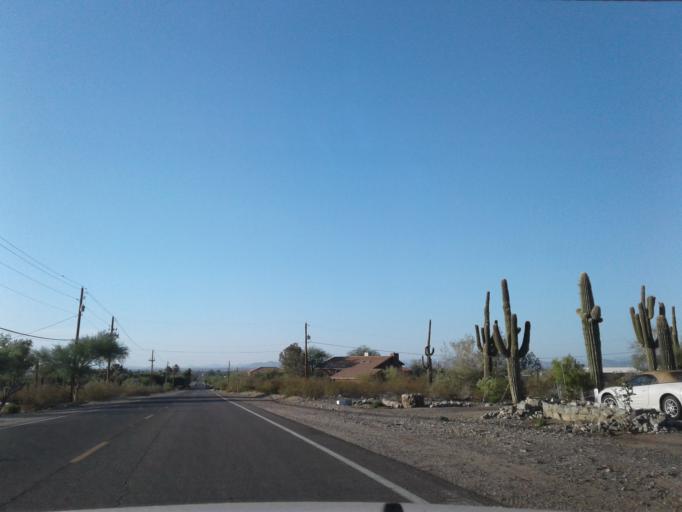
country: US
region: Arizona
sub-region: Maricopa County
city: Laveen
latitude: 33.3531
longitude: -112.1177
